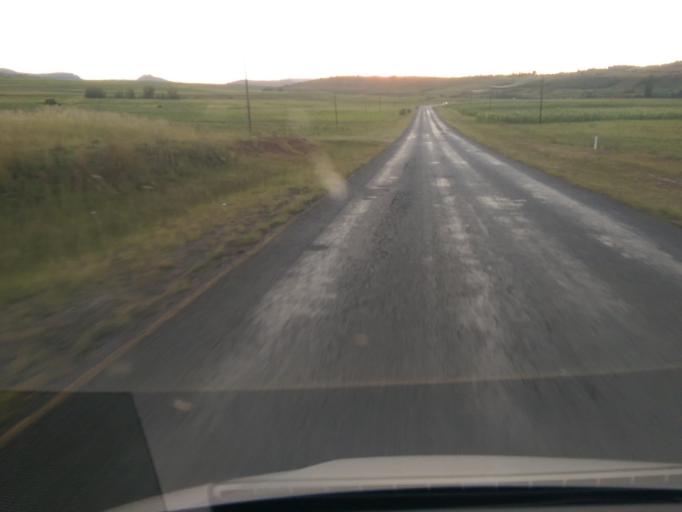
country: LS
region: Maseru
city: Nako
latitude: -29.4372
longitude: 27.6979
